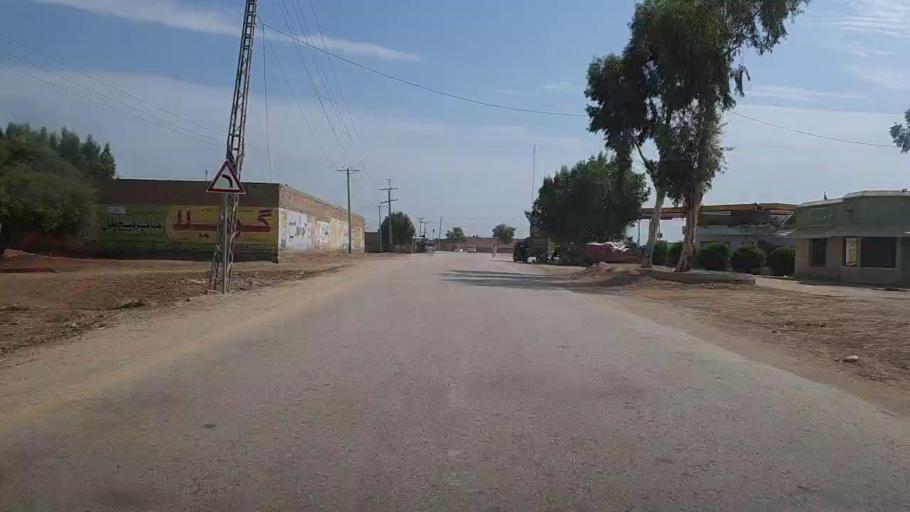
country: PK
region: Sindh
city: Thul
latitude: 28.2324
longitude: 68.7907
